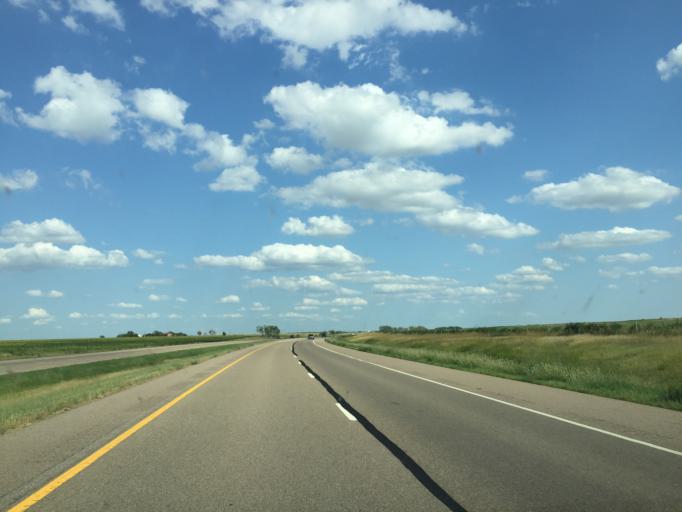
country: US
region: Kansas
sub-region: Gove County
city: Gove
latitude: 39.0964
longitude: -100.3248
